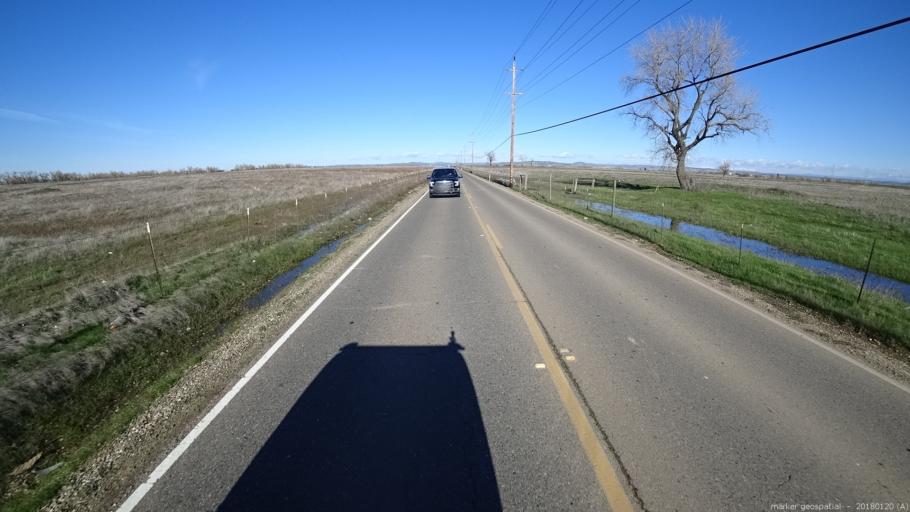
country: US
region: California
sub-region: Sacramento County
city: Gold River
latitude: 38.5858
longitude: -121.1841
